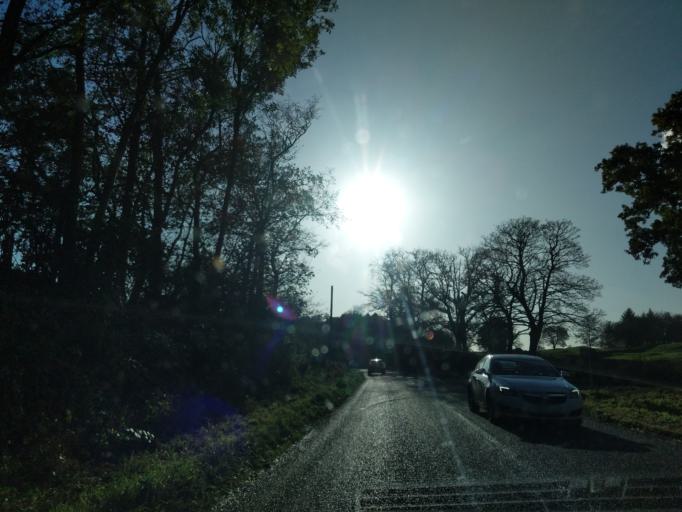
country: GB
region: Scotland
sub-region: Dumfries and Galloway
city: Kirkcudbright
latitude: 54.9058
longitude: -4.0077
